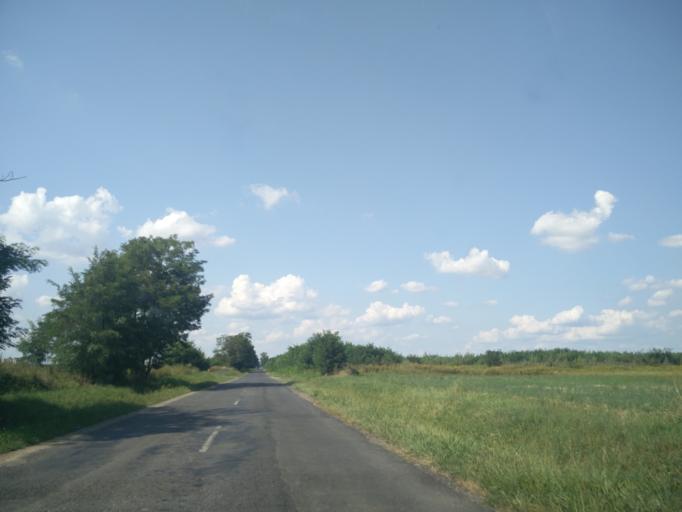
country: HU
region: Zala
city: Zalaegerszeg
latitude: 46.8745
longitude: 16.7941
